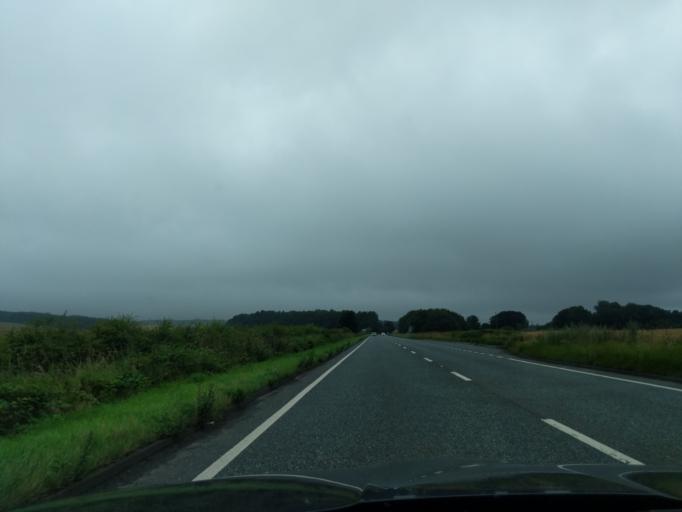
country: GB
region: England
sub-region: Northumberland
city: Ellingham
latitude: 55.4877
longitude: -1.7283
